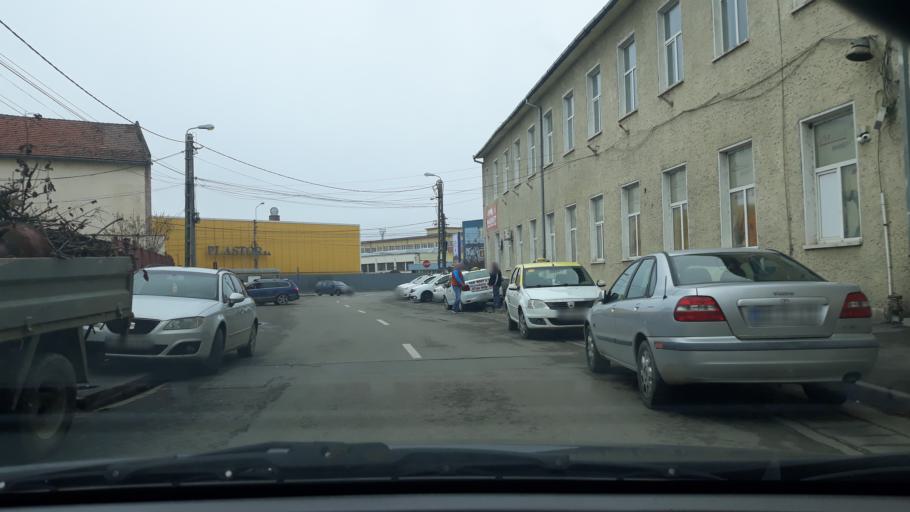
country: RO
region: Bihor
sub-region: Comuna Sanmartin
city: Sanmartin
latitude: 47.0460
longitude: 21.9674
